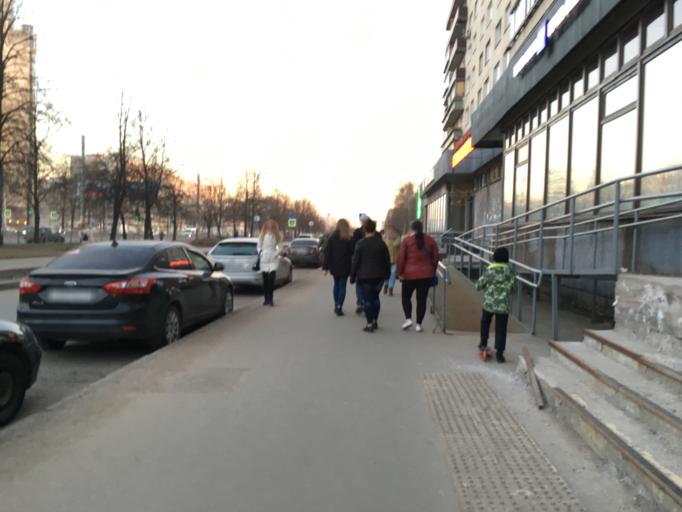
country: RU
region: St.-Petersburg
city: Grazhdanka
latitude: 60.0327
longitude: 30.4169
